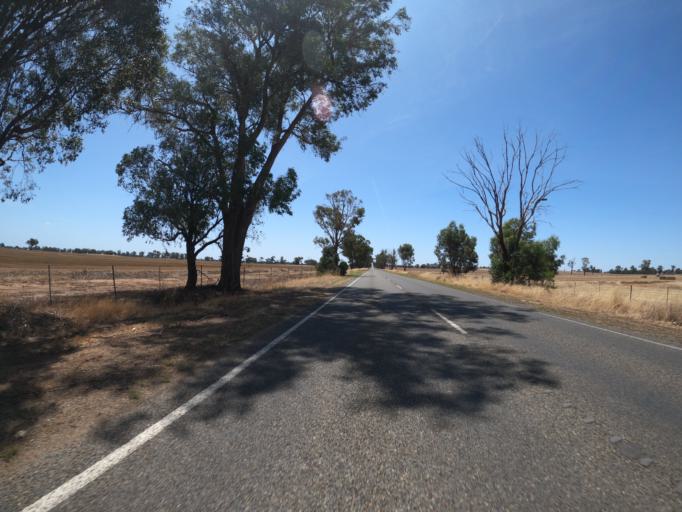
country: AU
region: Victoria
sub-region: Moira
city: Yarrawonga
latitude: -36.0636
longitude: 145.9954
